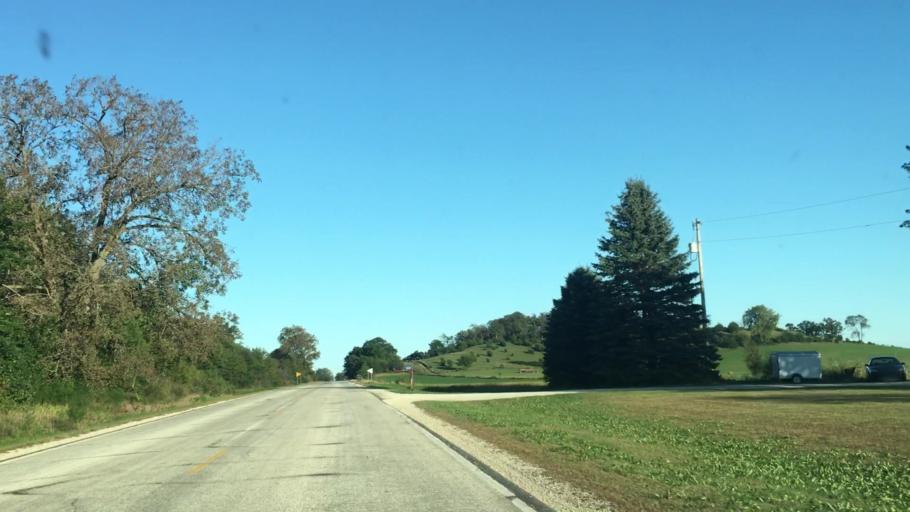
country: US
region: Minnesota
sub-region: Fillmore County
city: Chatfield
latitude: 43.8415
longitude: -92.0861
